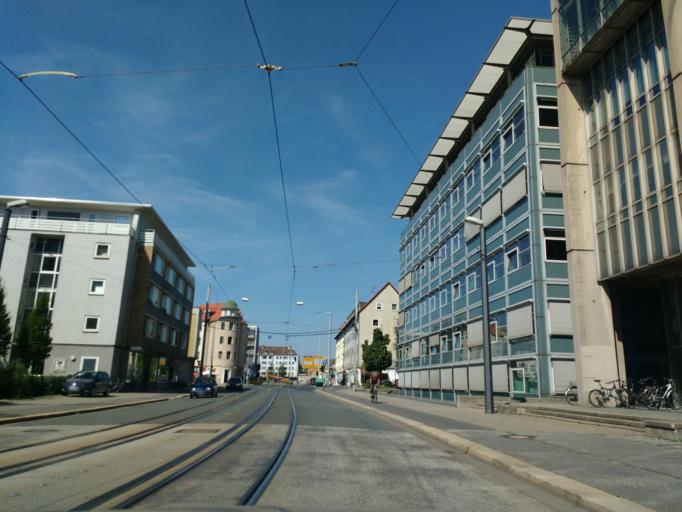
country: DE
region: Lower Saxony
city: Braunschweig
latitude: 52.2729
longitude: 10.5249
